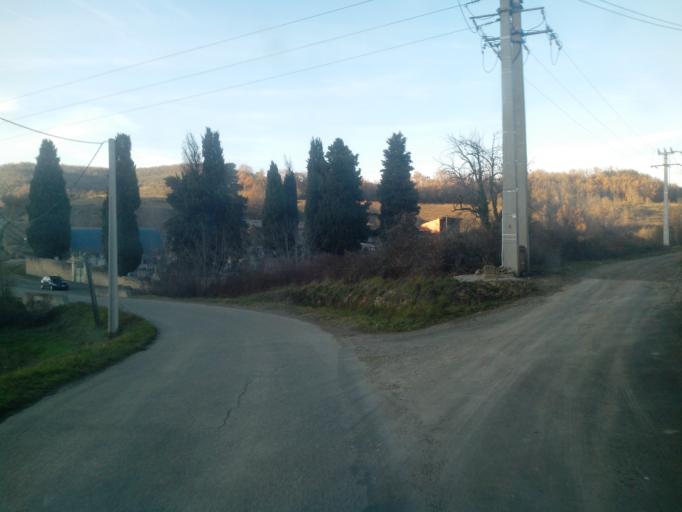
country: FR
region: Languedoc-Roussillon
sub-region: Departement de l'Aude
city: Esperaza
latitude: 42.9403
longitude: 2.1887
